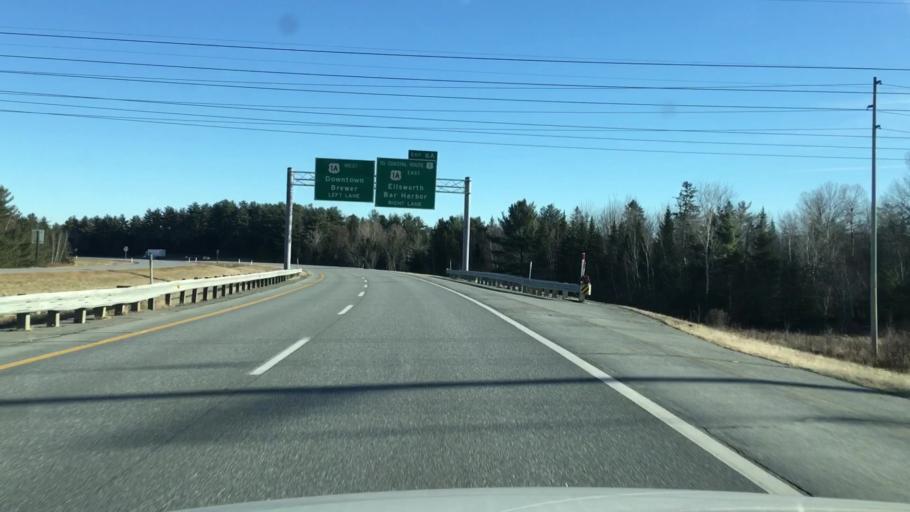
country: US
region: Maine
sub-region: Penobscot County
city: Brewer
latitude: 44.7683
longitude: -68.7354
